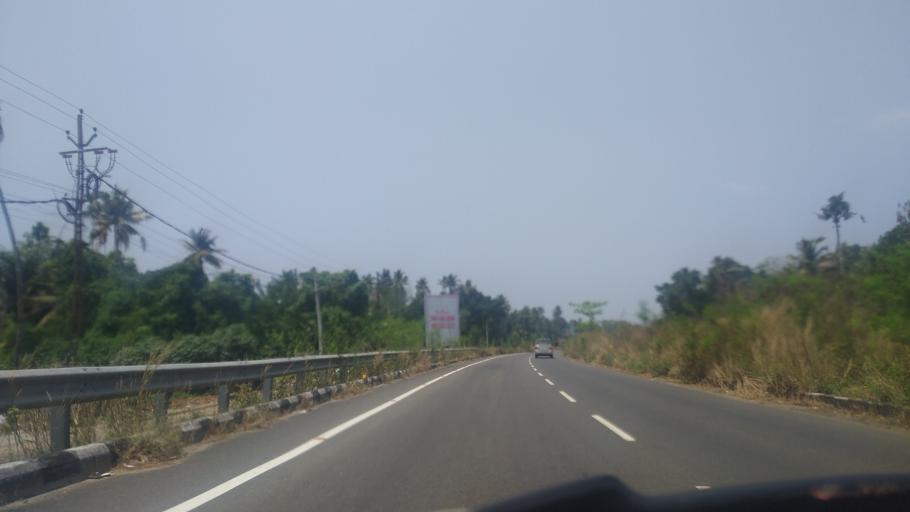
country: IN
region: Kerala
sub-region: Thrissur District
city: Kodungallur
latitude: 10.2172
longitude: 76.1965
